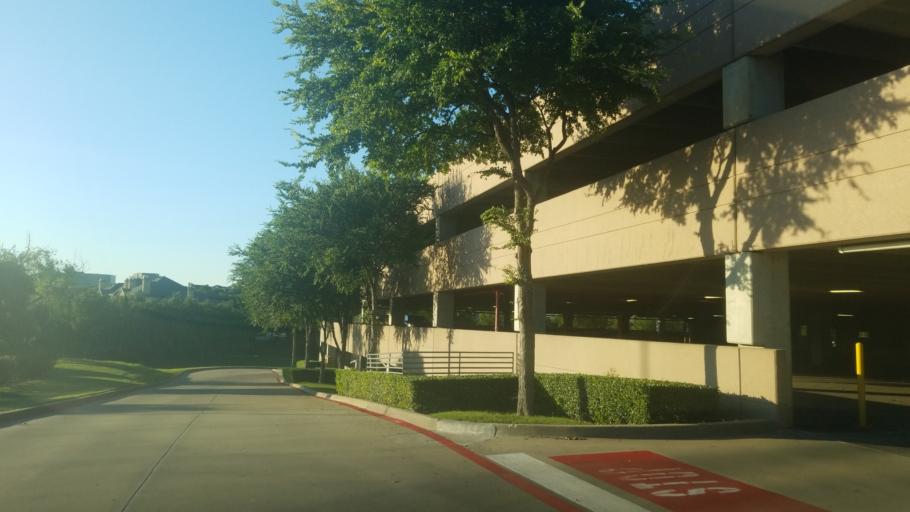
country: US
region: Texas
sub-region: Dallas County
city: Irving
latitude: 32.8784
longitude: -96.9612
